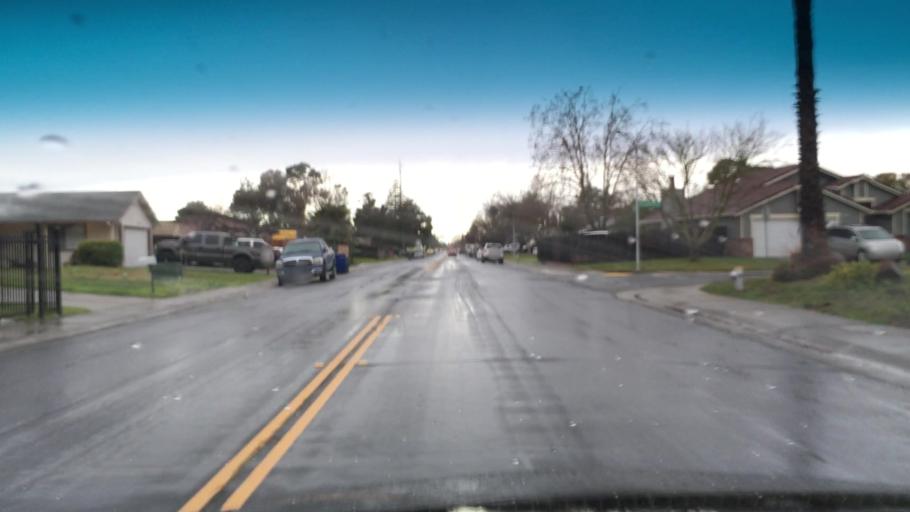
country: US
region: California
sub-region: Sacramento County
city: Laguna
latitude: 38.4579
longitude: -121.4357
